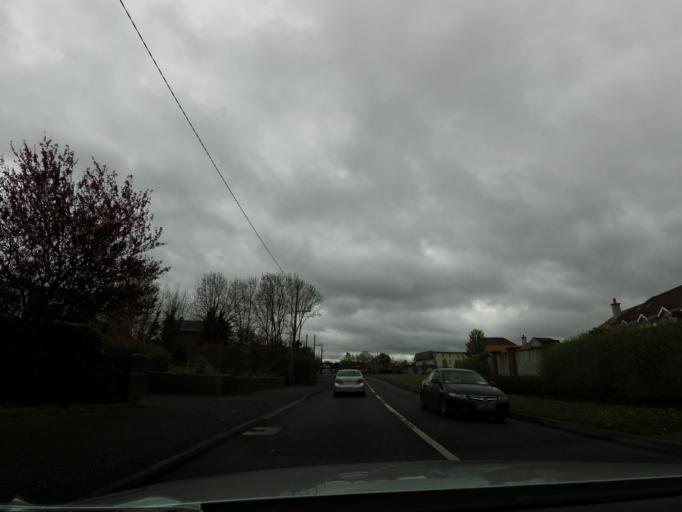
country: IE
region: Leinster
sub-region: Kilkenny
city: Kilkenny
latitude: 52.6692
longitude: -7.2662
